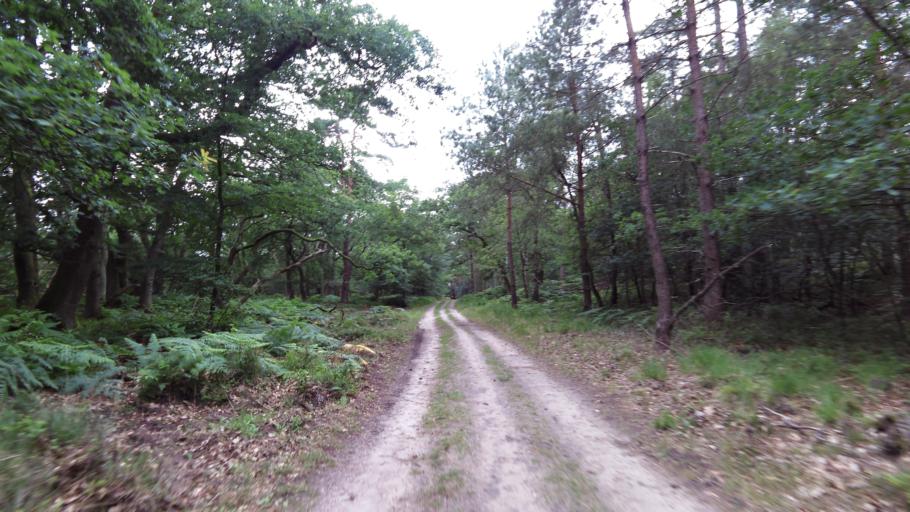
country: NL
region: Gelderland
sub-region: Gemeente Apeldoorn
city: Apeldoorn
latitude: 52.2092
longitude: 5.8735
